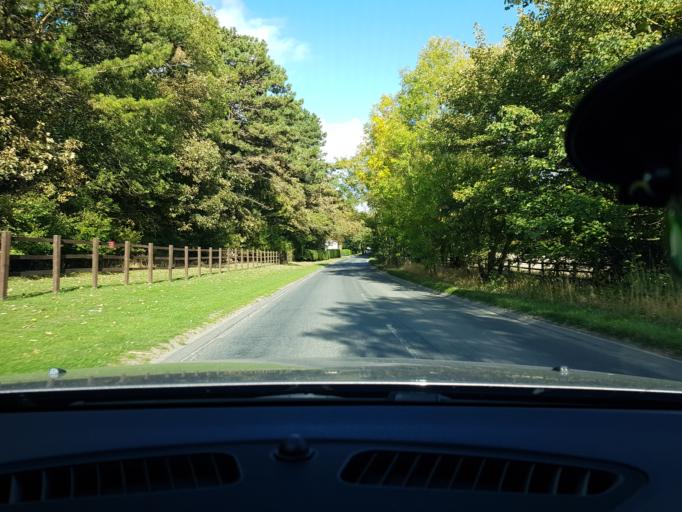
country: GB
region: England
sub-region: Borough of Swindon
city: Wanborough
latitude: 51.5275
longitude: -1.6740
